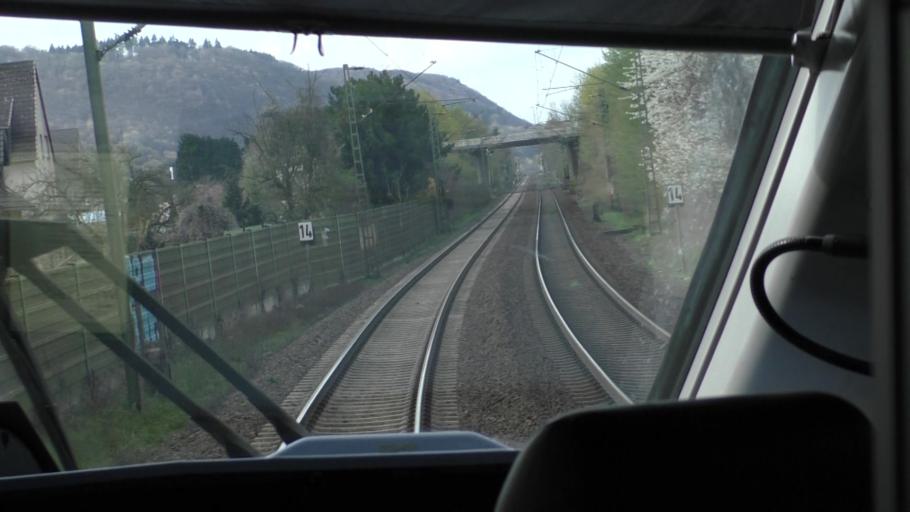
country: DE
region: Rheinland-Pfalz
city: Leutesdorf
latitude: 50.4486
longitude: 7.3721
